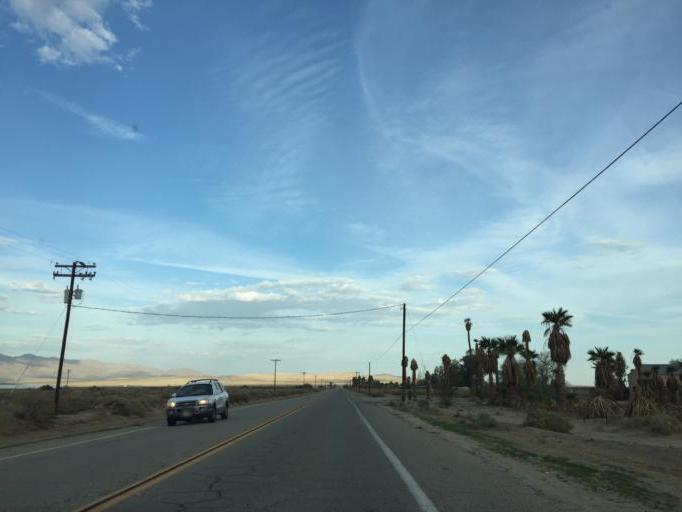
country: US
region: California
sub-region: San Diego County
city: Borrego Springs
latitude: 33.2569
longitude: -116.3429
